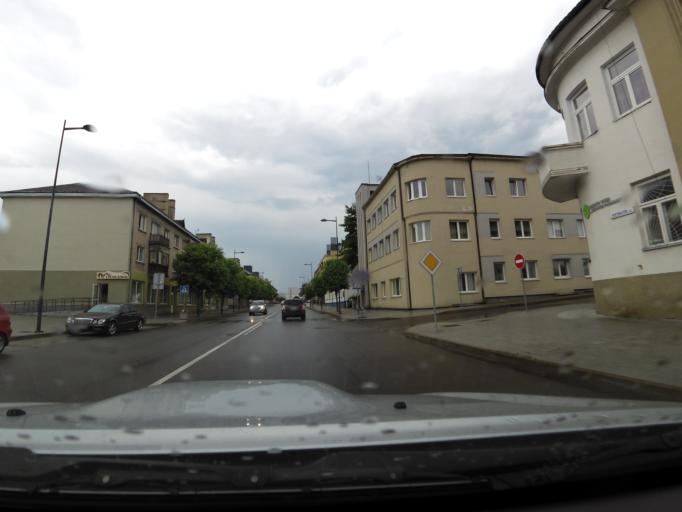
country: LT
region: Marijampoles apskritis
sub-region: Marijampole Municipality
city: Marijampole
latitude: 54.5536
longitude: 23.3488
